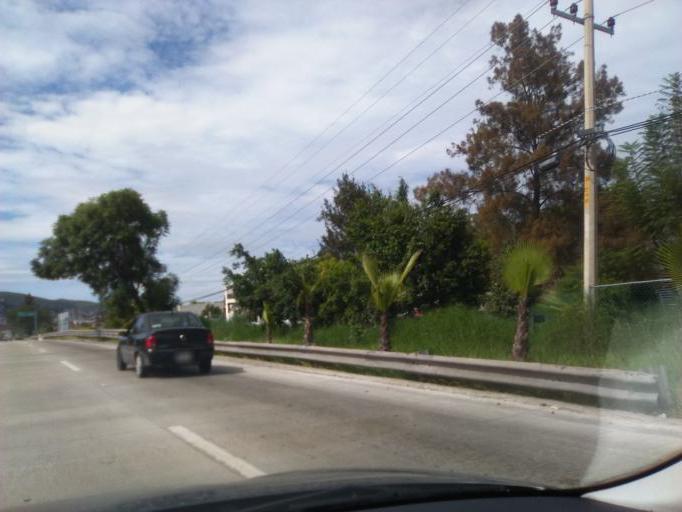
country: MX
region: Guerrero
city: Chilpancingo de los Bravos
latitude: 17.5319
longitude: -99.4941
